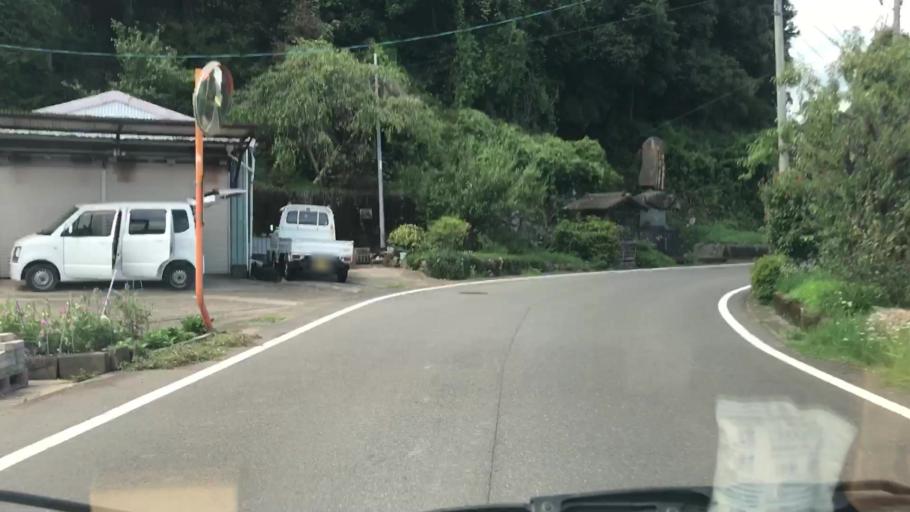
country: JP
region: Saga Prefecture
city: Kashima
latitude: 33.1181
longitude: 130.0701
